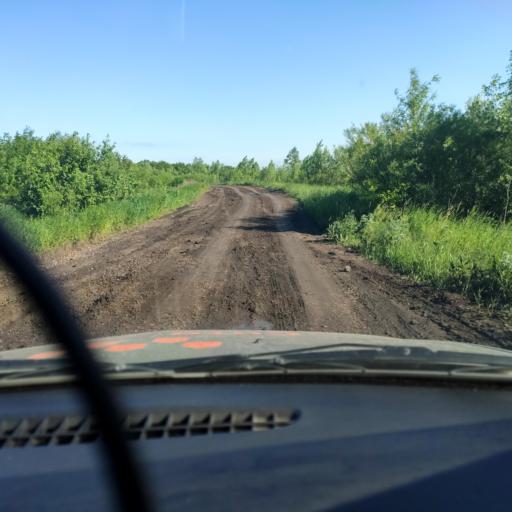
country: RU
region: Bashkortostan
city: Avdon
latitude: 54.5766
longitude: 55.8483
